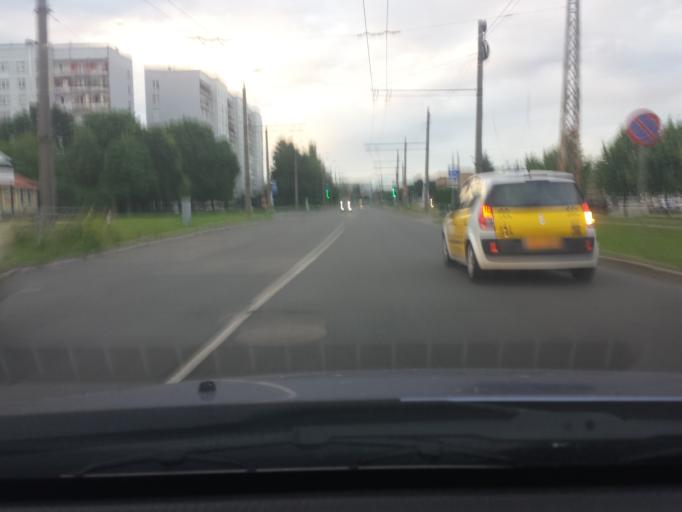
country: LV
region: Stopini
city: Ulbroka
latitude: 56.9583
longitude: 24.2383
